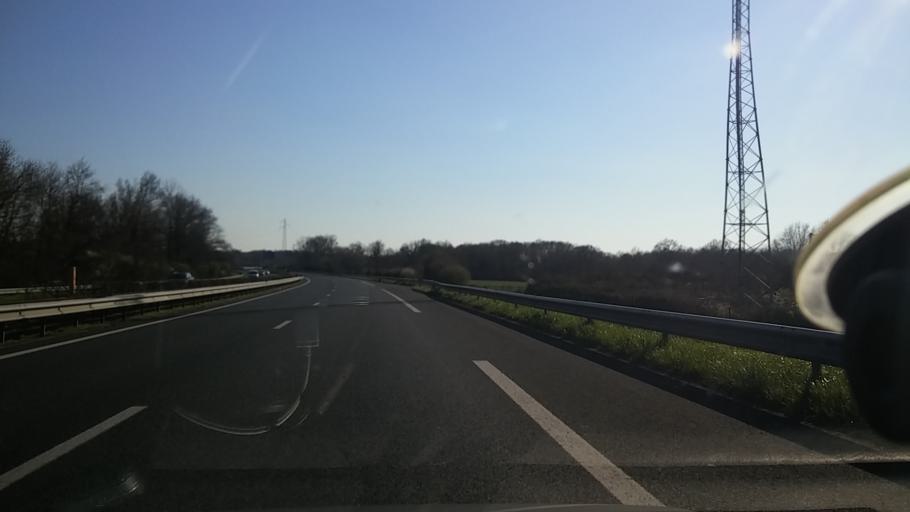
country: FR
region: Centre
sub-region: Departement de l'Indre
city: Luant
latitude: 46.7055
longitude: 1.5862
